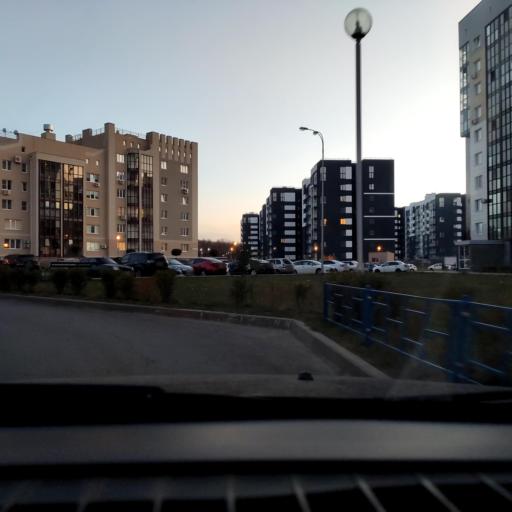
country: RU
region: Samara
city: Tol'yatti
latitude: 53.5291
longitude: 49.3420
